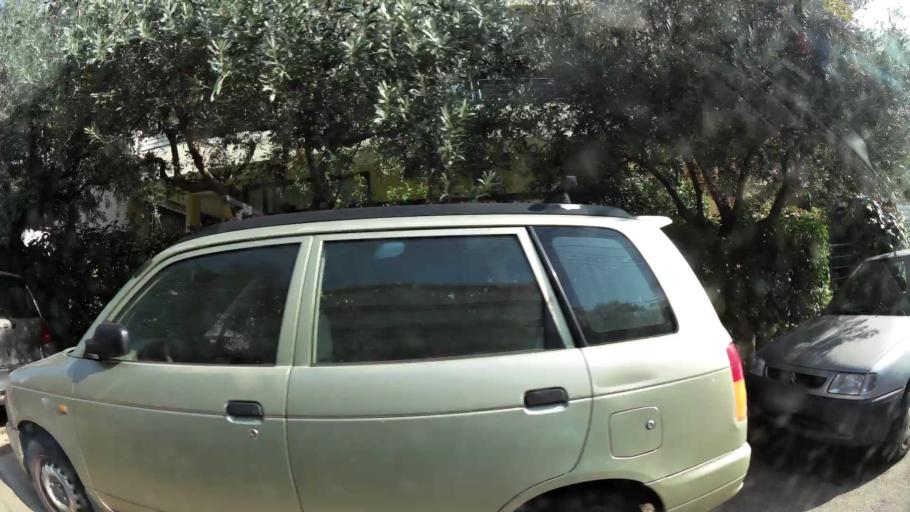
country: GR
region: Attica
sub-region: Nomos Attikis
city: Zografos
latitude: 37.9780
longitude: 23.7948
